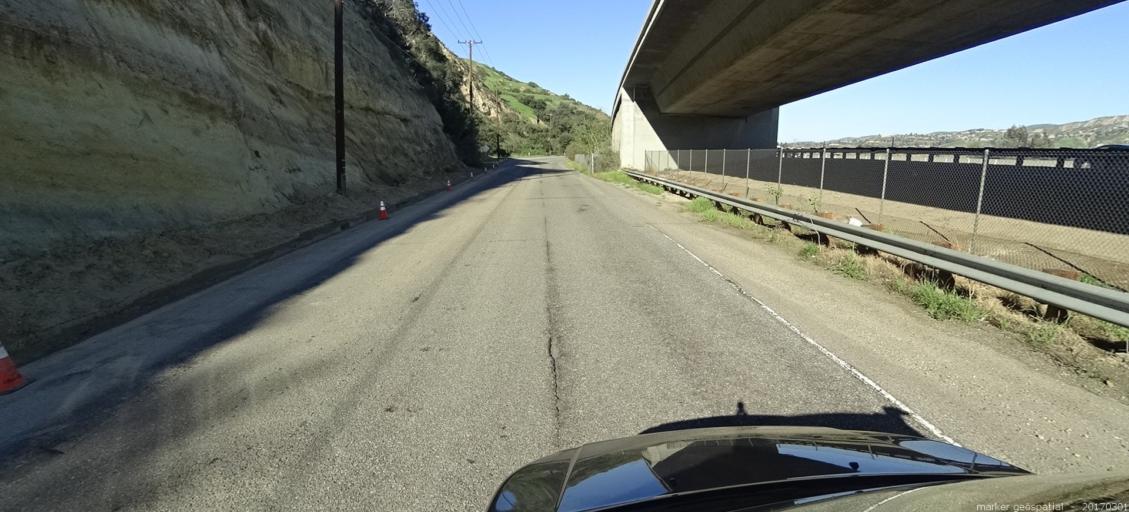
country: US
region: California
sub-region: Orange County
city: Yorba Linda
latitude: 33.8668
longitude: -117.7244
